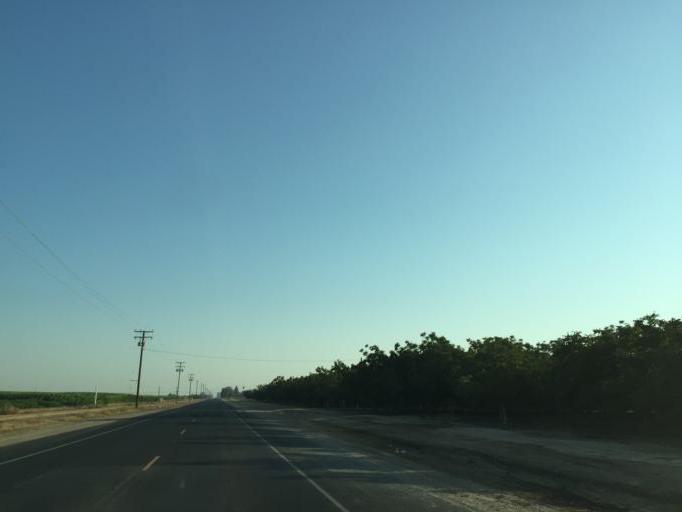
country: US
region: California
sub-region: Tulare County
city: Ivanhoe
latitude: 36.4230
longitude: -119.2959
